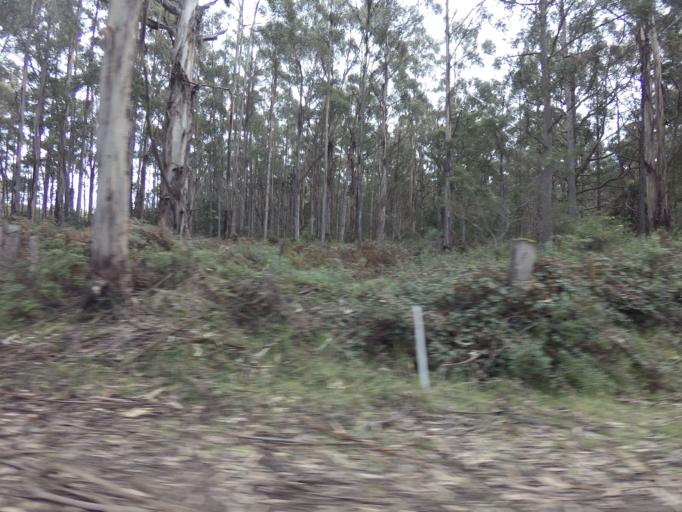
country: AU
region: Tasmania
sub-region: Huon Valley
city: Geeveston
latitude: -43.4192
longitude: 147.0142
